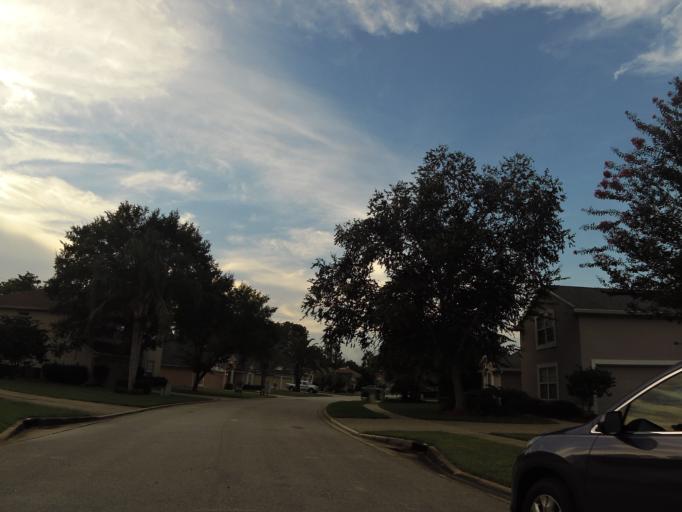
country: US
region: Florida
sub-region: Saint Johns County
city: Palm Valley
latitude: 30.2094
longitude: -81.5196
